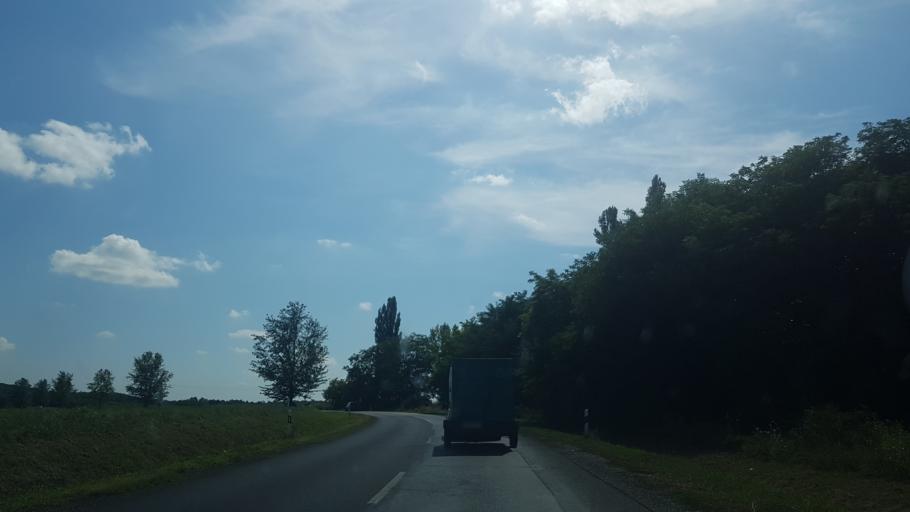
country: HU
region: Somogy
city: Bohonye
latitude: 46.4661
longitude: 17.3756
